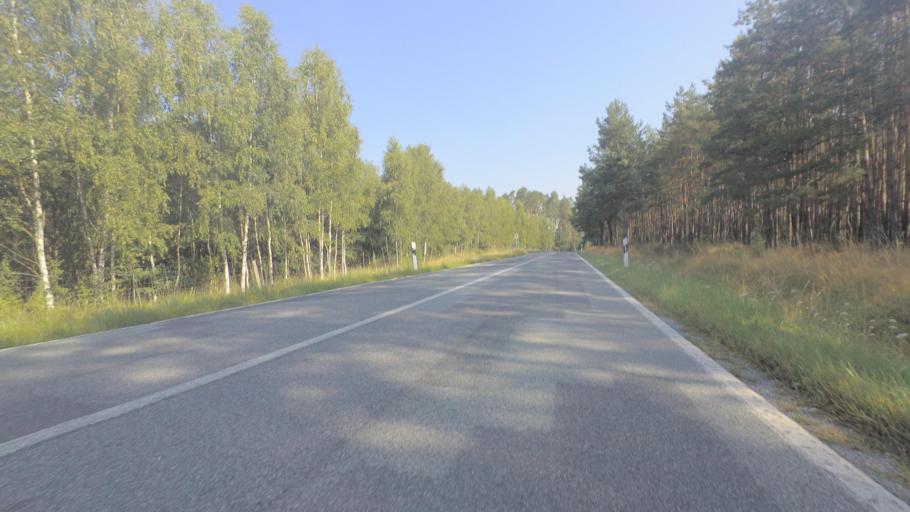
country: DE
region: Mecklenburg-Vorpommern
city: Malchow
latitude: 53.5715
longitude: 12.4562
